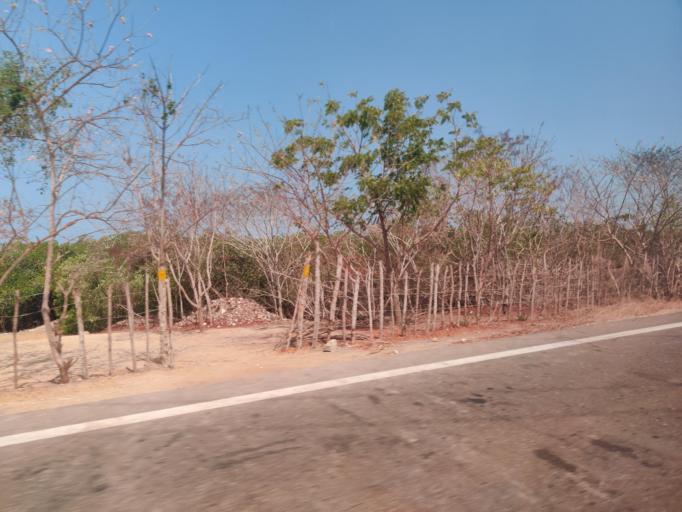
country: CO
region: Bolivar
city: Turbana
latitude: 10.1680
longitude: -75.6500
